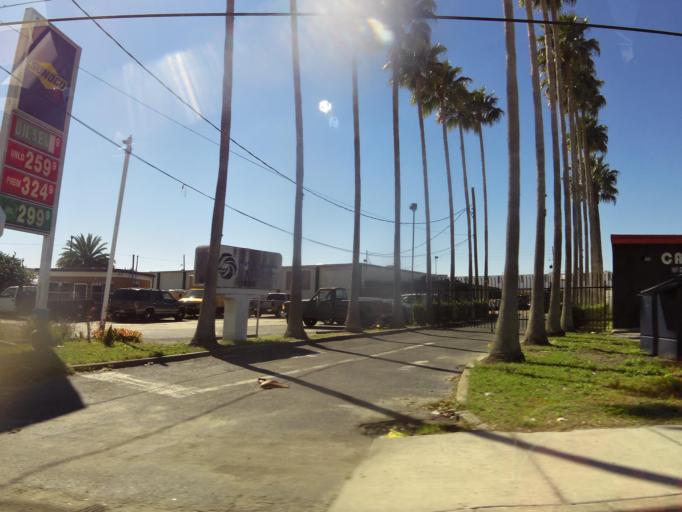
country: US
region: Florida
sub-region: Orange County
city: Fairview Shores
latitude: 28.5690
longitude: -81.4039
